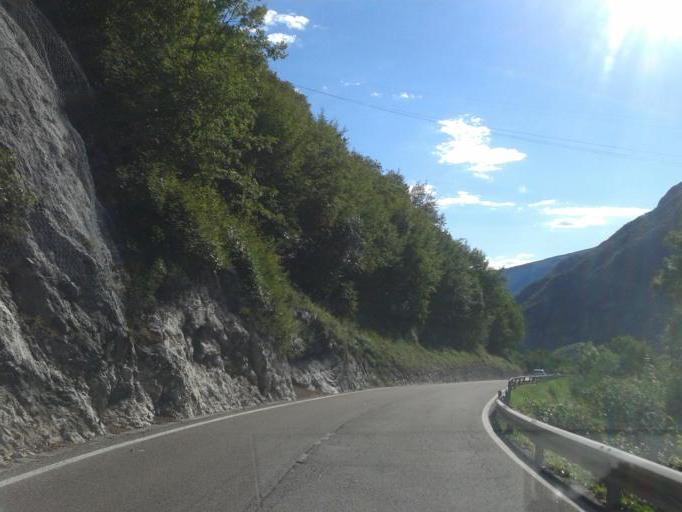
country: IT
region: Trentino-Alto Adige
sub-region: Provincia di Trento
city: Molina di Ledro
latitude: 45.8692
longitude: 10.7863
